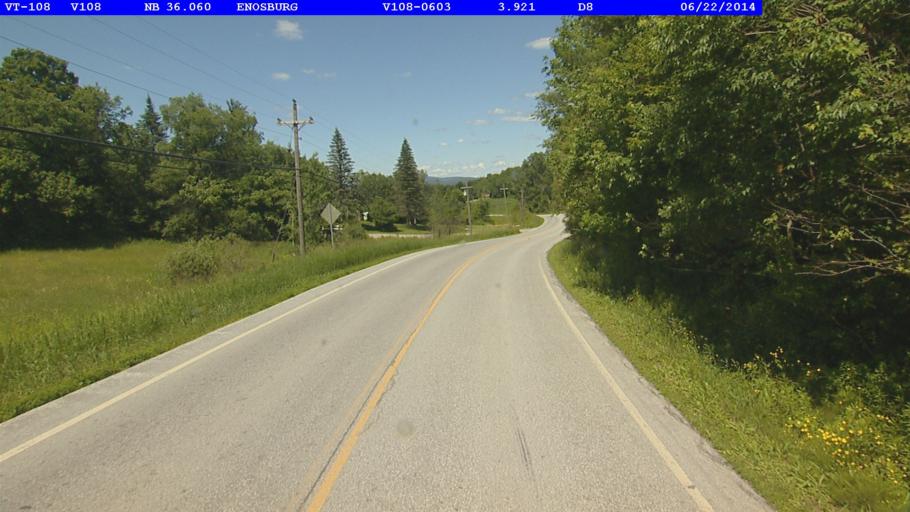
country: US
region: Vermont
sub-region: Franklin County
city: Enosburg Falls
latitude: 44.8921
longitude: -72.8018
